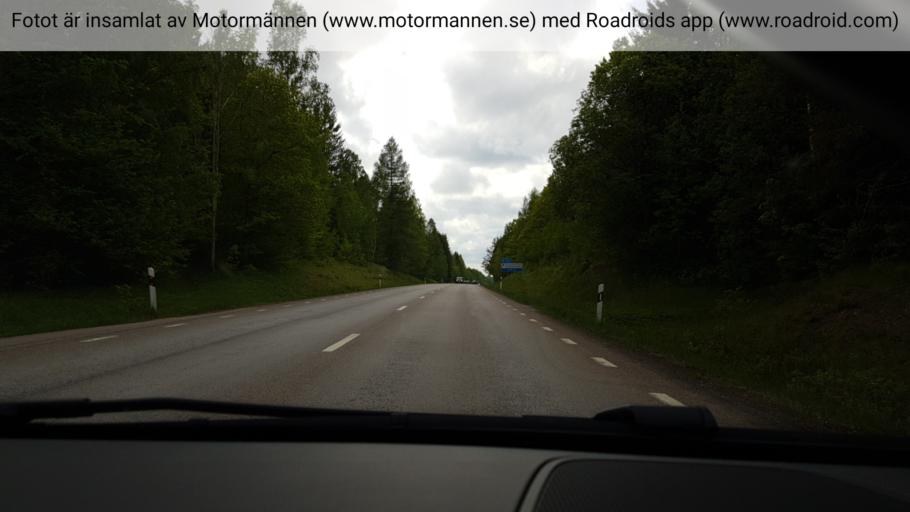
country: SE
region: Uppsala
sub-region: Osthammars Kommun
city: Osterbybruk
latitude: 60.1945
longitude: 17.8566
